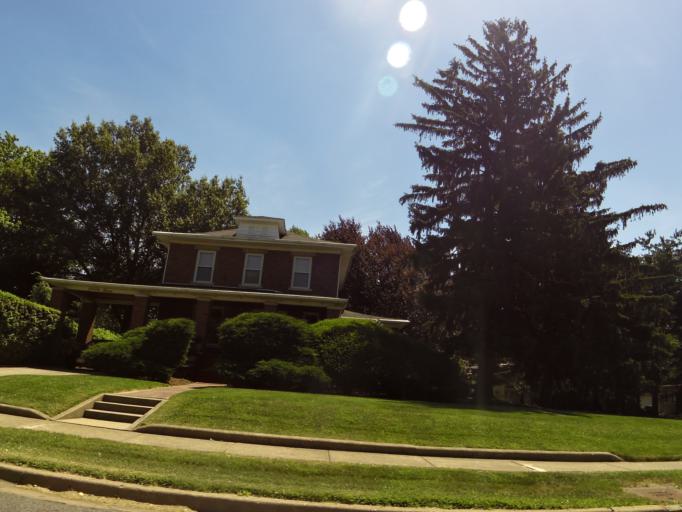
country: US
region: Illinois
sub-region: Vermilion County
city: Danville
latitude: 40.1595
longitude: -87.6304
